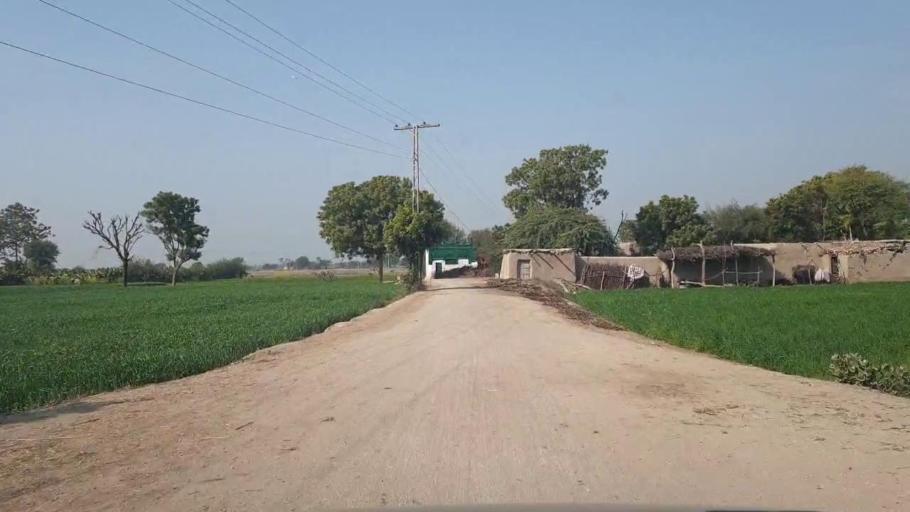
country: PK
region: Sindh
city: Tando Adam
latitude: 25.7471
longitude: 68.5845
